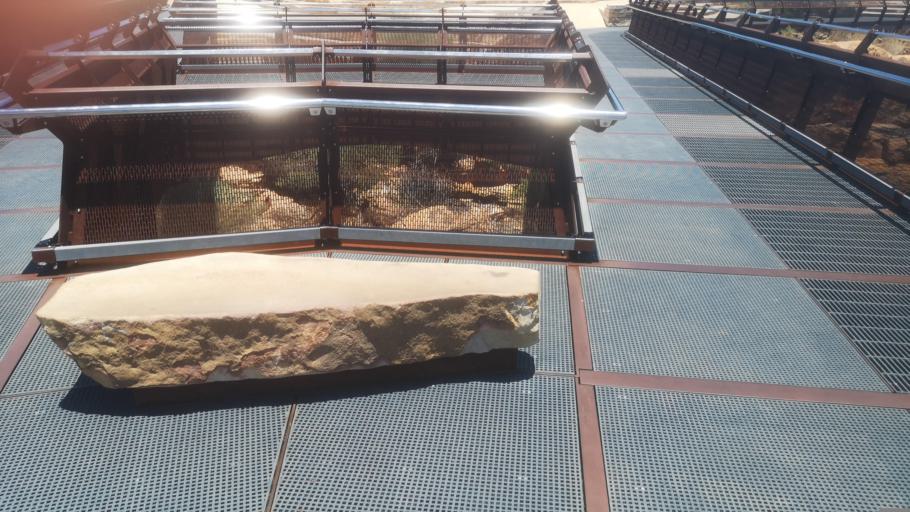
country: AU
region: Western Australia
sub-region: Northampton Shire
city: Kalbarri
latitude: -27.5545
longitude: 114.4343
